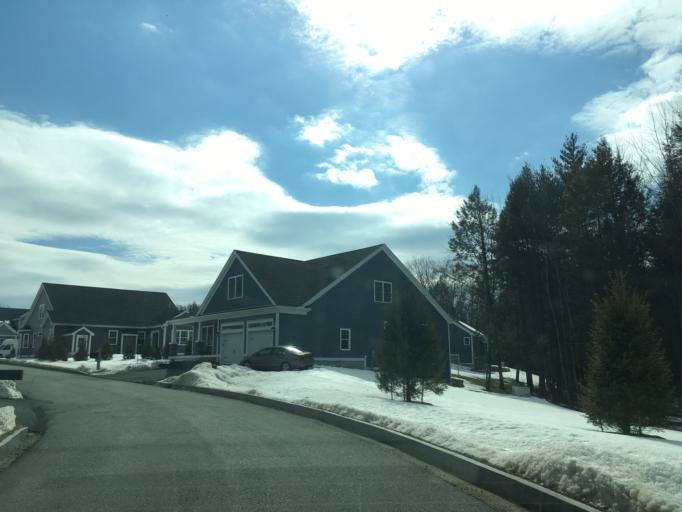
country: US
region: New Hampshire
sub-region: Rockingham County
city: Exeter
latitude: 42.9832
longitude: -70.8916
